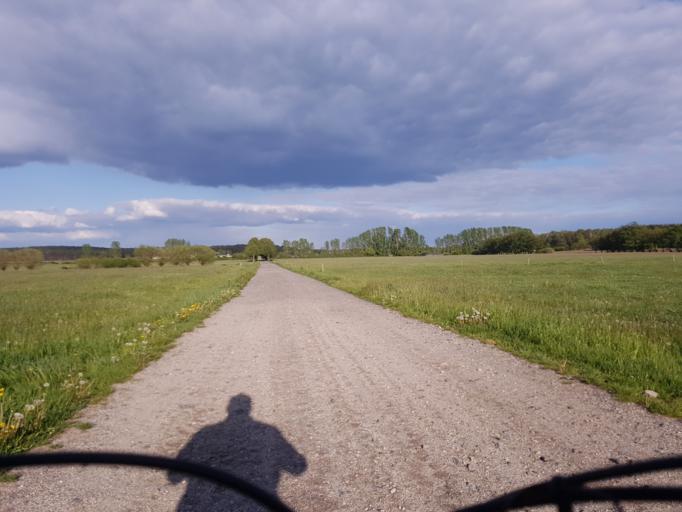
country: DE
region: Brandenburg
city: Schilda
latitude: 51.5618
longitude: 13.3980
